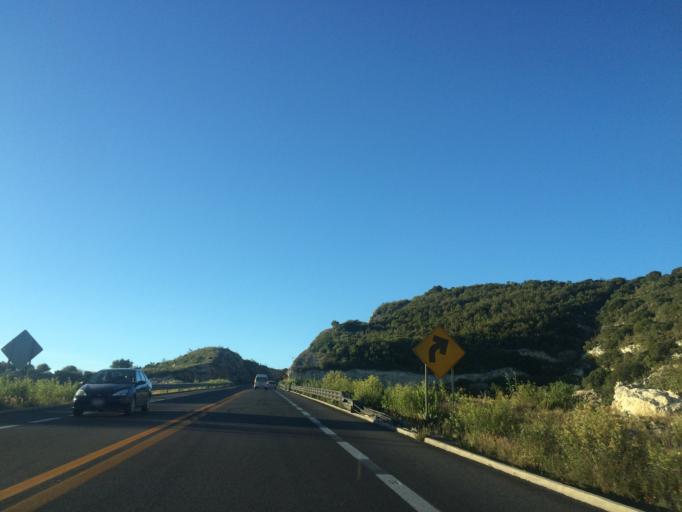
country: MX
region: Puebla
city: Chapuco
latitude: 18.6561
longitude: -97.4550
